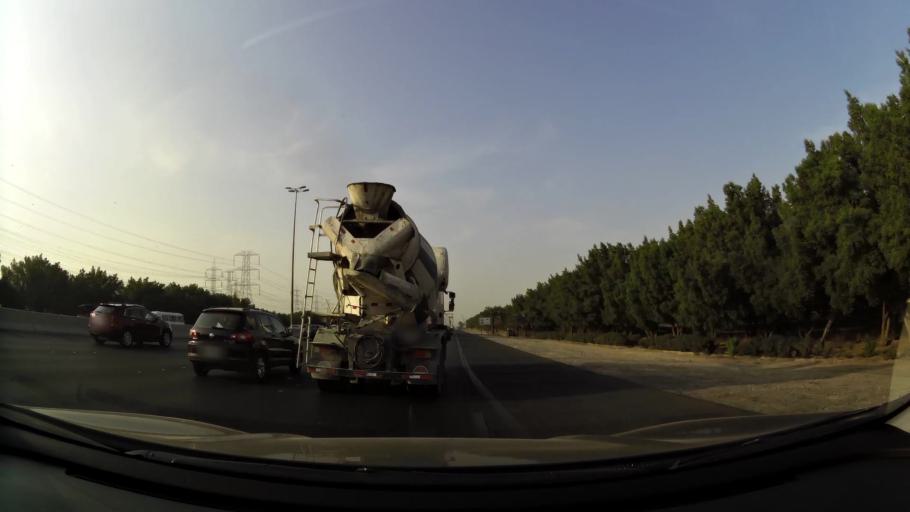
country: KW
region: Mubarak al Kabir
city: Sabah as Salim
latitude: 29.2244
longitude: 48.0546
